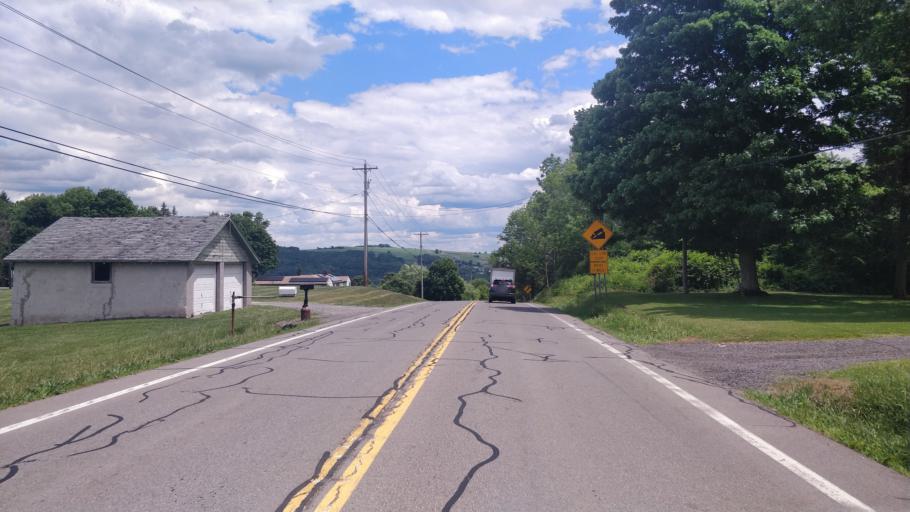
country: US
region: New York
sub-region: Cortland County
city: Homer
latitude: 42.6375
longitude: -76.2033
